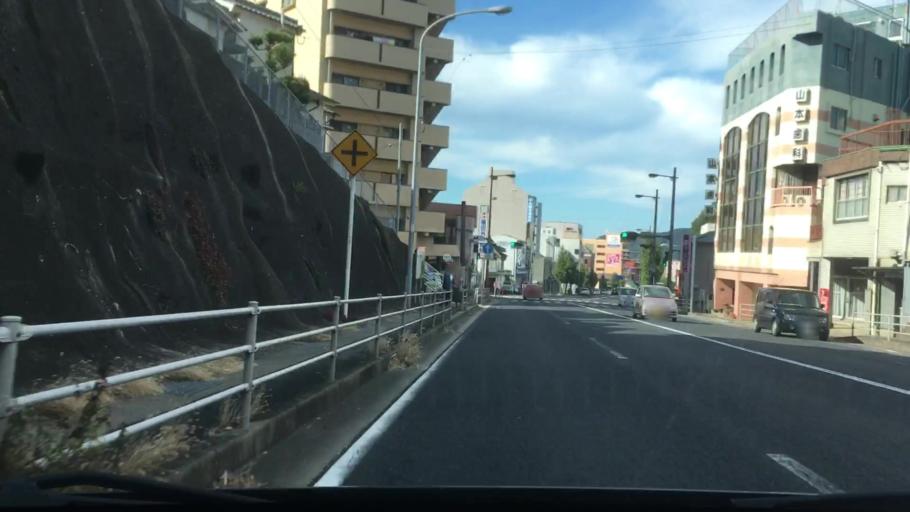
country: JP
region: Nagasaki
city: Sasebo
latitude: 33.1596
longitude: 129.7406
